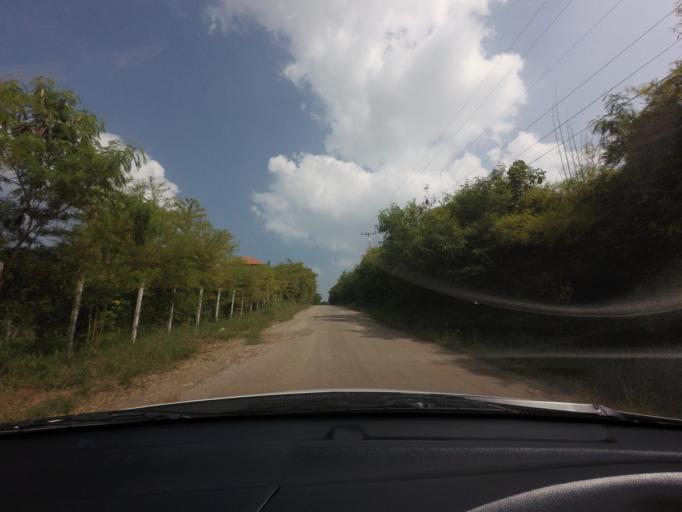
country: TH
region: Nakhon Ratchasima
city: Pak Chong
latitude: 14.5438
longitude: 101.5924
